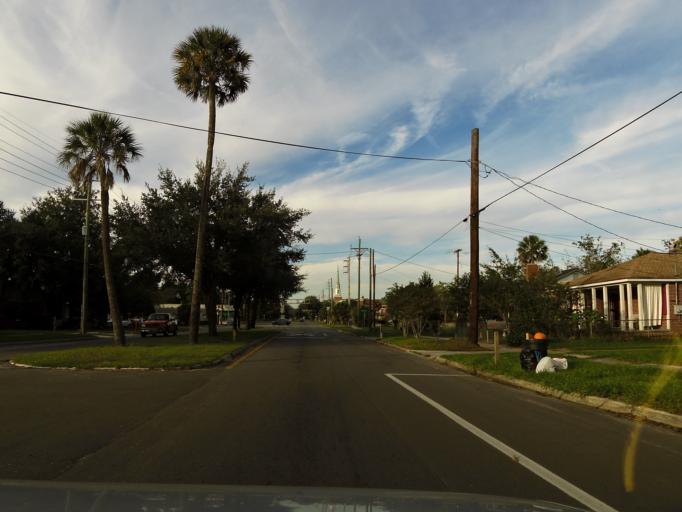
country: US
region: Florida
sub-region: Duval County
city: Jacksonville
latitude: 30.3764
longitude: -81.6567
